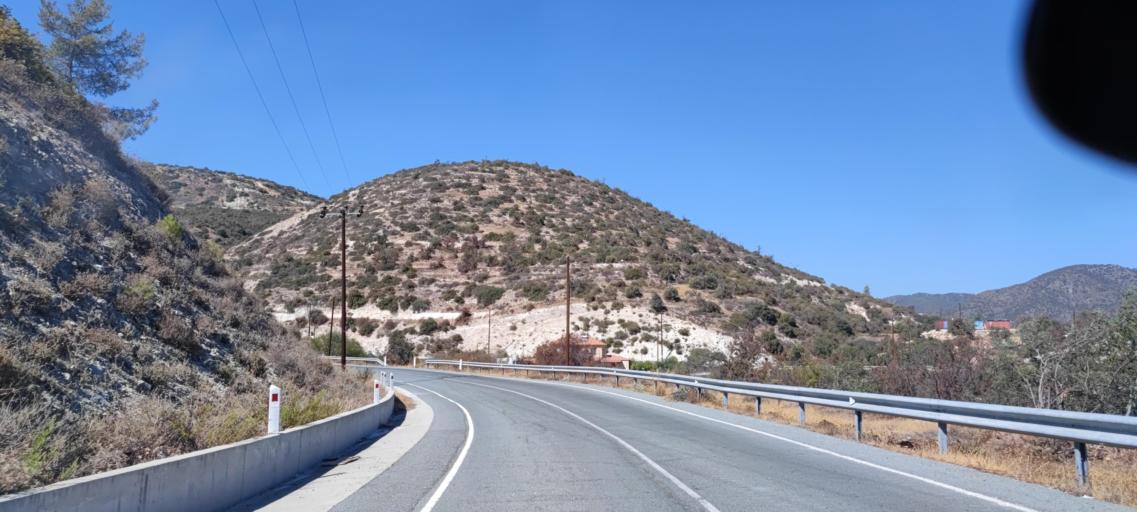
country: CY
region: Limassol
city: Mouttagiaka
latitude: 34.7687
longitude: 33.0528
